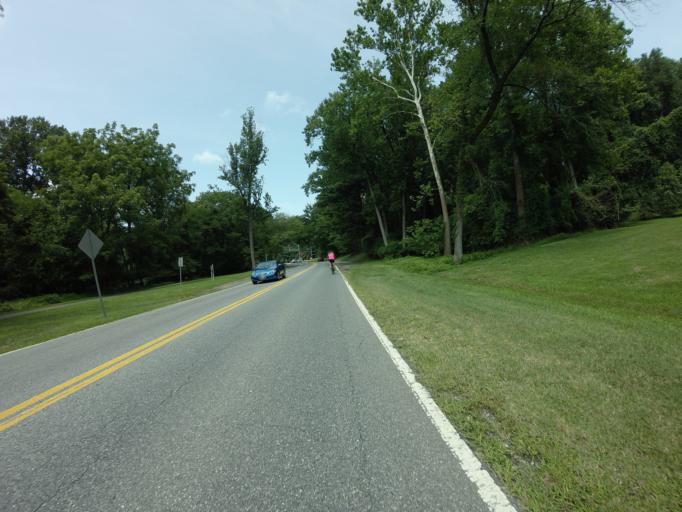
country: US
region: Maryland
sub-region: Montgomery County
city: South Kensington
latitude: 39.0115
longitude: -77.0897
